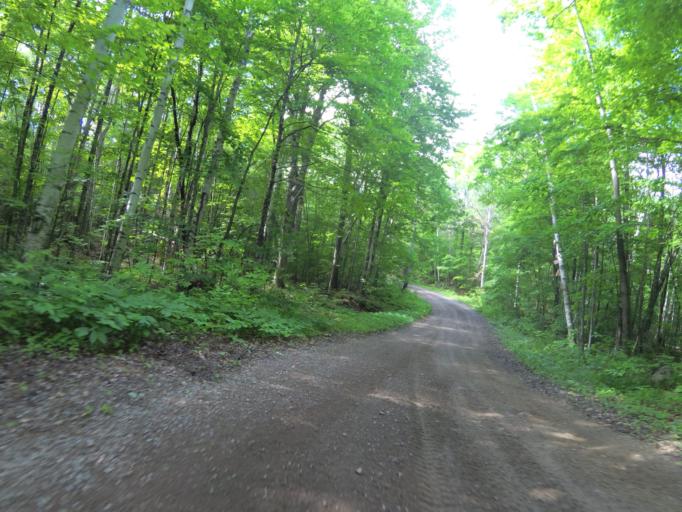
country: CA
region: Ontario
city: Renfrew
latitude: 45.1492
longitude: -76.8811
